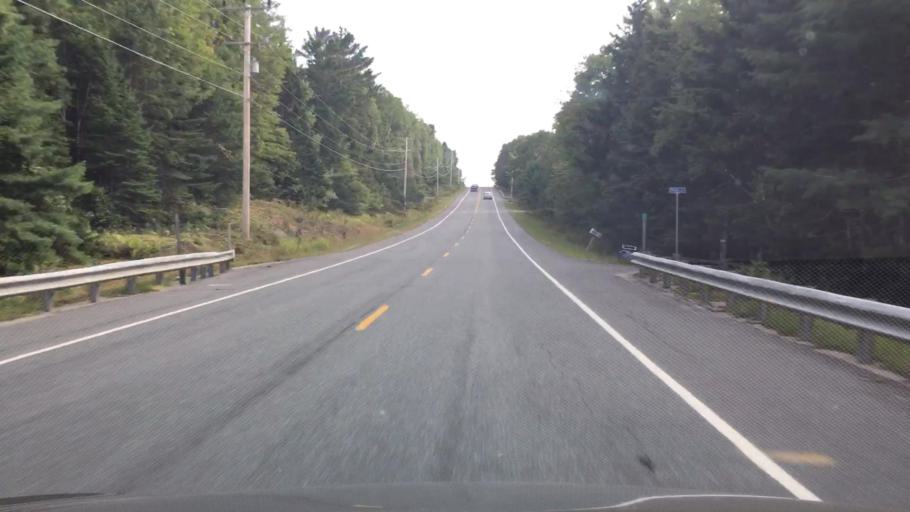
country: US
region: Maine
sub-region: Hancock County
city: Surry
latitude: 44.4827
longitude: -68.5162
